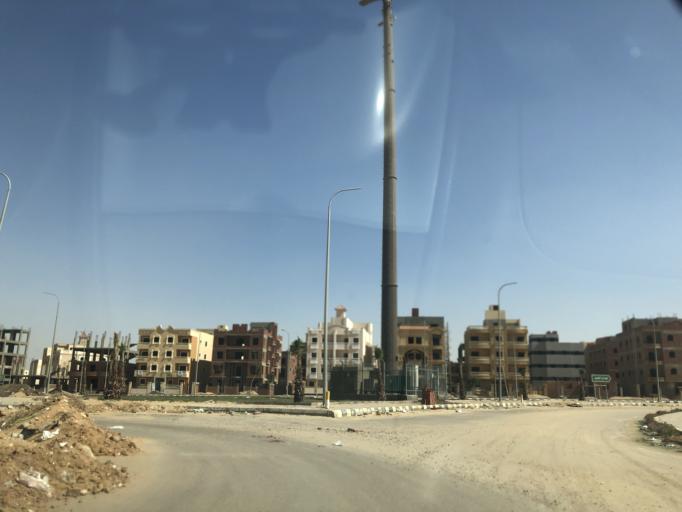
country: EG
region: Al Jizah
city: Madinat Sittah Uktubar
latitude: 29.9253
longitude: 31.0437
